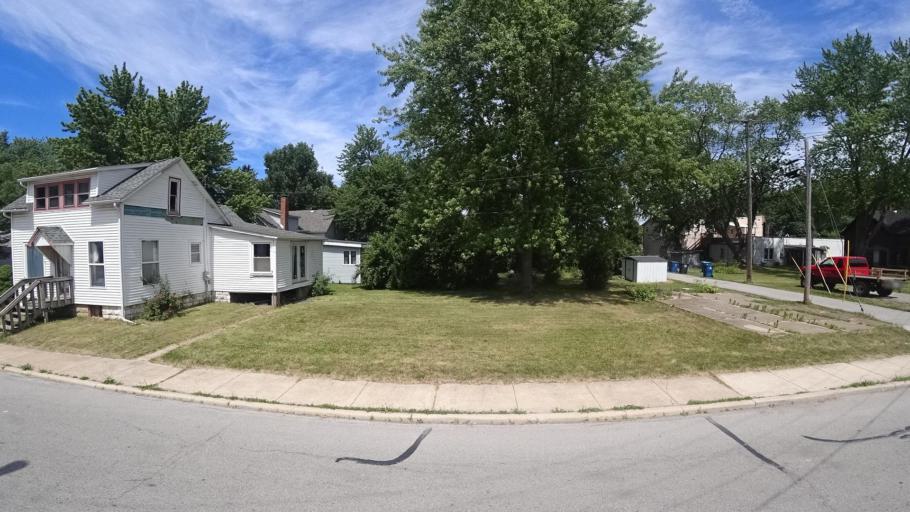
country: US
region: Indiana
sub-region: Porter County
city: Porter
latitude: 41.6148
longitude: -87.0752
